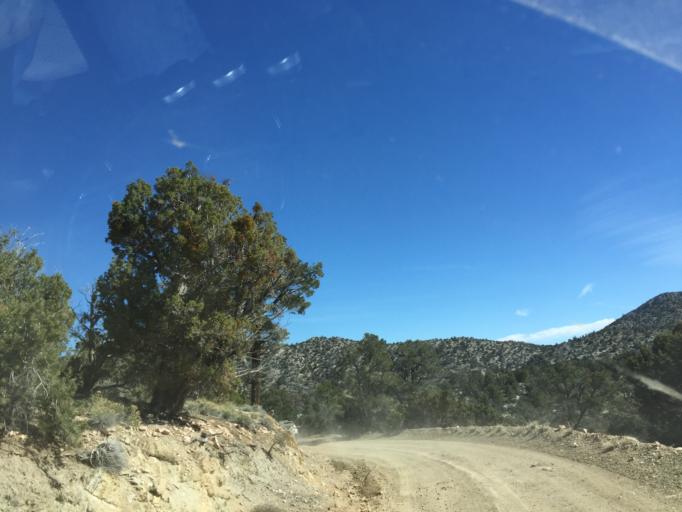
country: US
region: California
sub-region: San Bernardino County
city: Big Bear City
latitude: 34.2481
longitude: -116.7131
